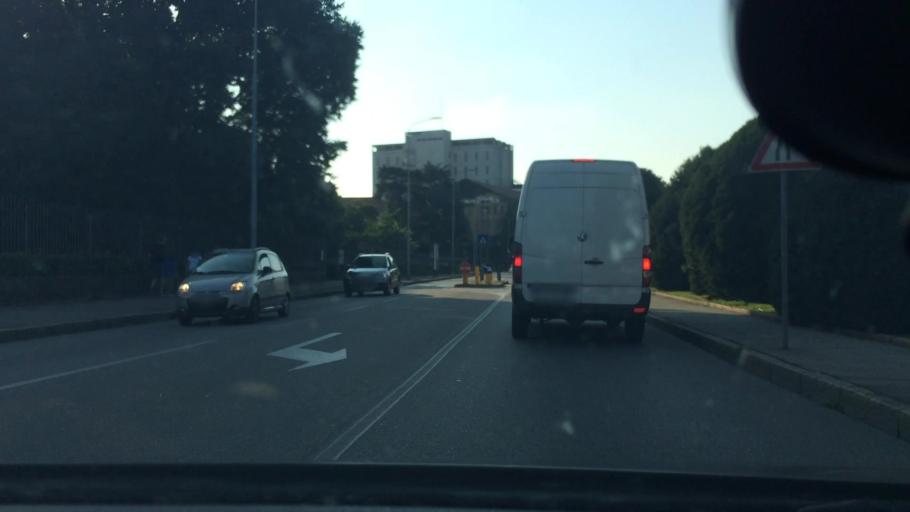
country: IT
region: Lombardy
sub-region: Citta metropolitana di Milano
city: Rho
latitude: 45.5321
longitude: 9.0427
